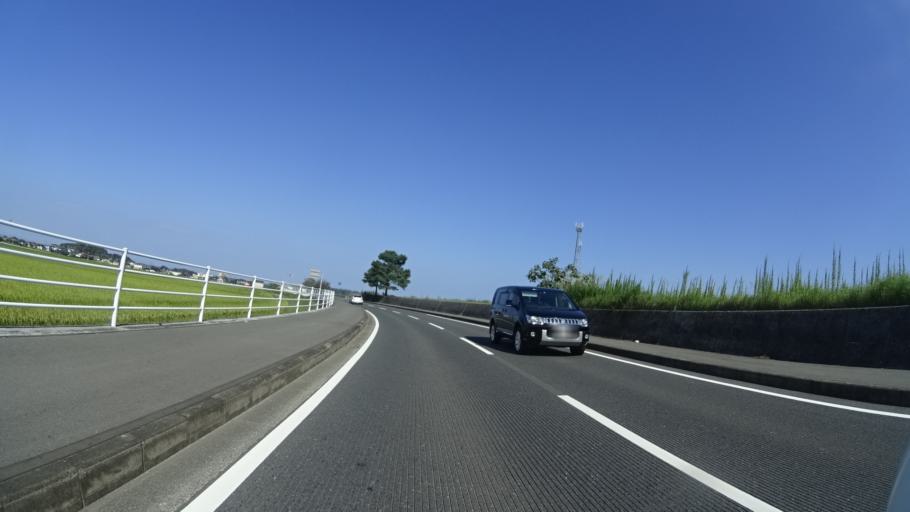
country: JP
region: Fukuoka
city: Shiida
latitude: 33.6447
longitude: 131.0619
